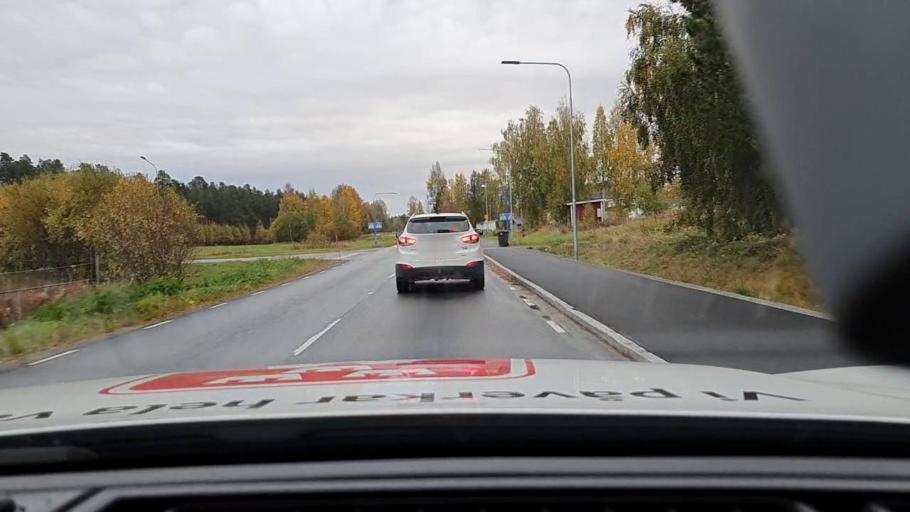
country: SE
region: Norrbotten
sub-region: Bodens Kommun
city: Saevast
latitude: 65.7720
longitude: 21.7009
